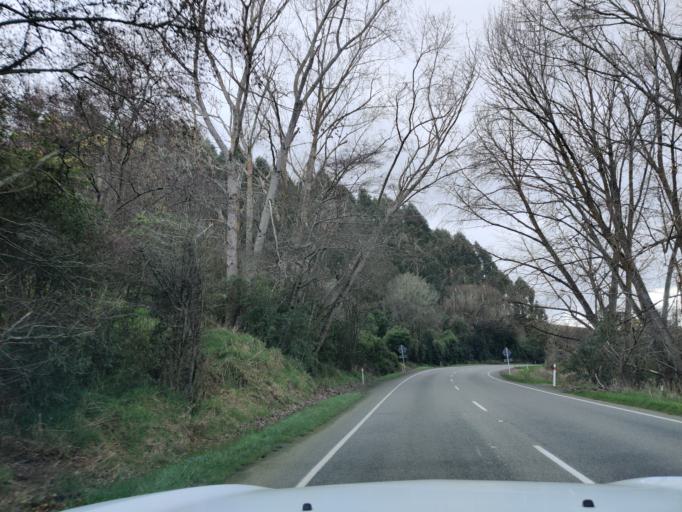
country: NZ
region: Manawatu-Wanganui
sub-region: Rangitikei District
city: Bulls
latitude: -39.9338
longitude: 175.5713
